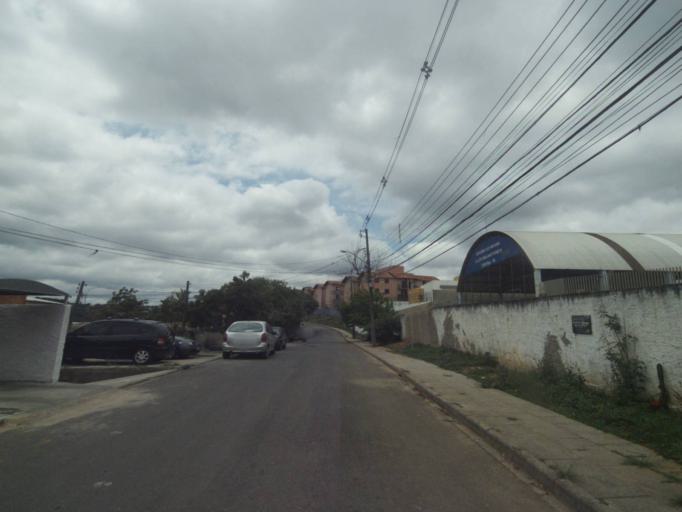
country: BR
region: Parana
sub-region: Curitiba
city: Curitiba
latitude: -25.3884
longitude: -49.2940
